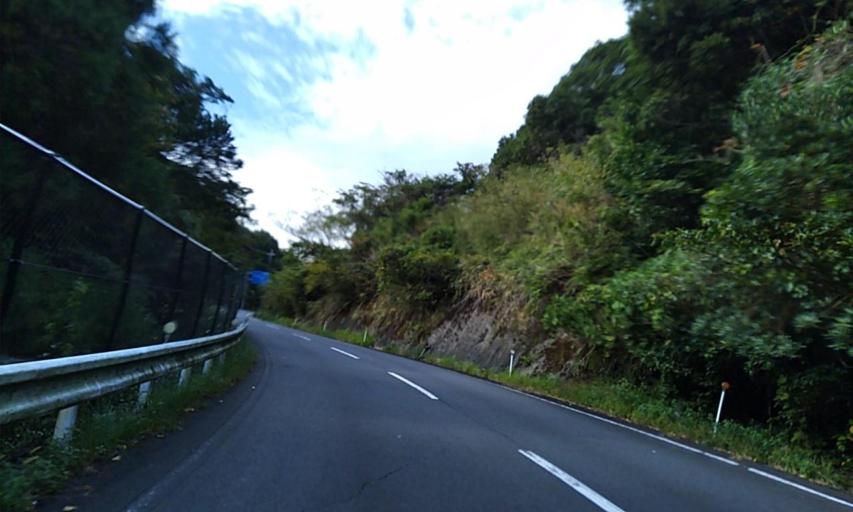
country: JP
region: Wakayama
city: Shingu
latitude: 33.4703
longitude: 135.8201
